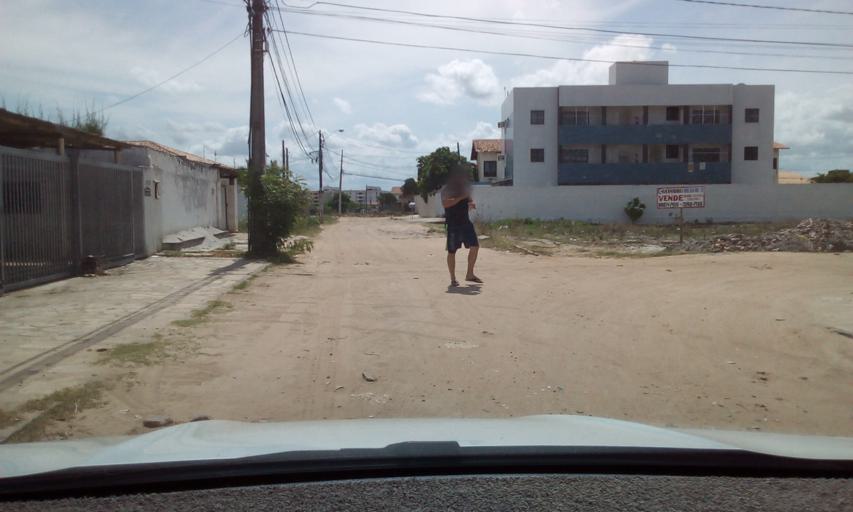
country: BR
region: Paraiba
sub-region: Joao Pessoa
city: Joao Pessoa
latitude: -7.0796
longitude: -34.8418
